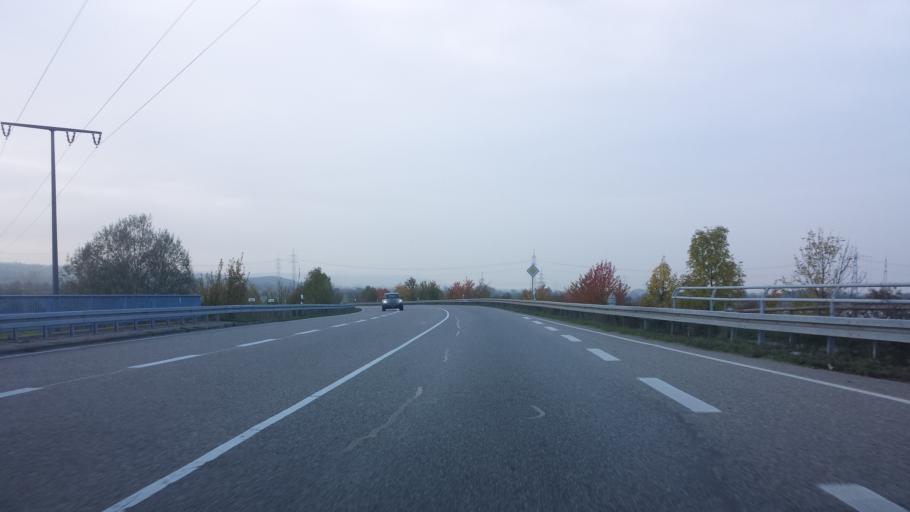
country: DE
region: Baden-Wuerttemberg
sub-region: Karlsruhe Region
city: Ubstadt-Weiher
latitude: 49.1687
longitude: 8.6196
